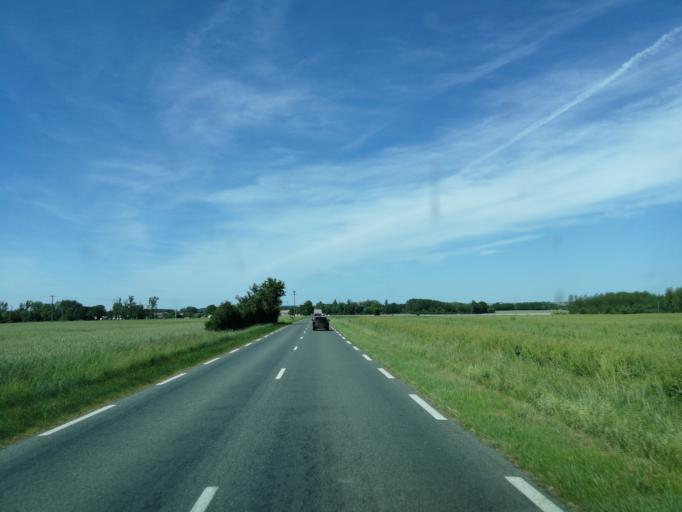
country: FR
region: Centre
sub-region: Departement d'Indre-et-Loire
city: Ligre
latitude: 47.0814
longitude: 0.1767
